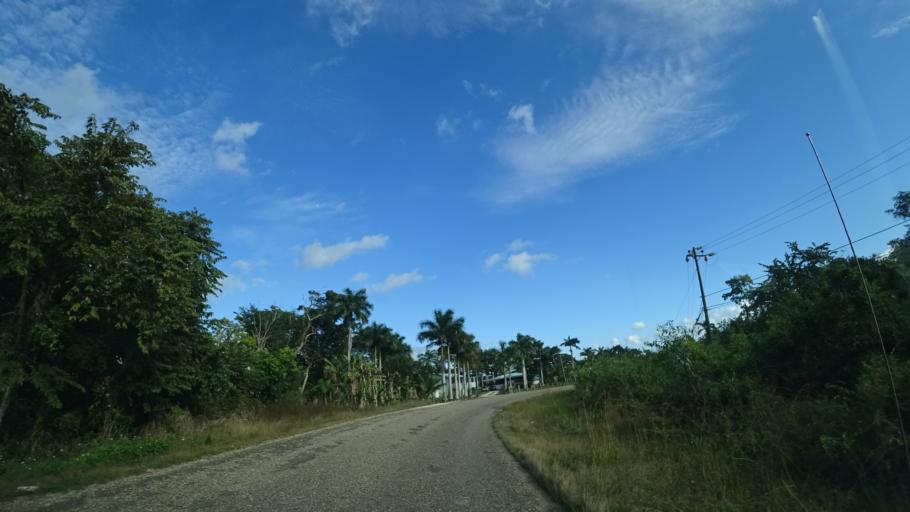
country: BZ
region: Belize
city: Belize City
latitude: 17.5713
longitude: -88.3890
